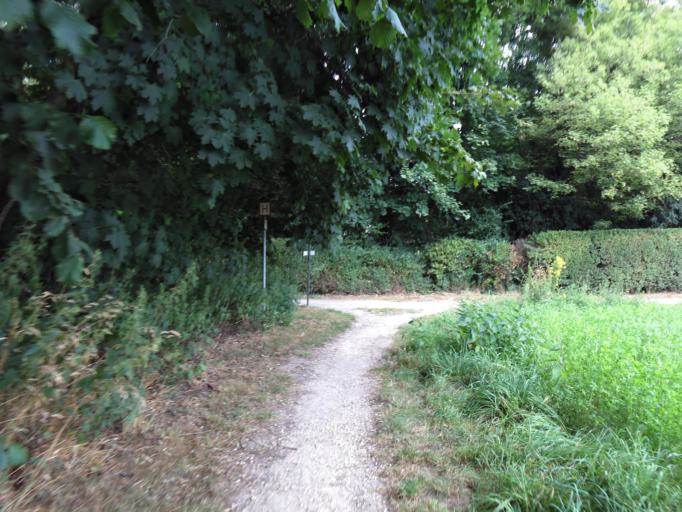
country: BE
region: Flanders
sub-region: Provincie Vlaams-Brabant
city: Dilbeek
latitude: 50.8405
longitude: 4.2740
